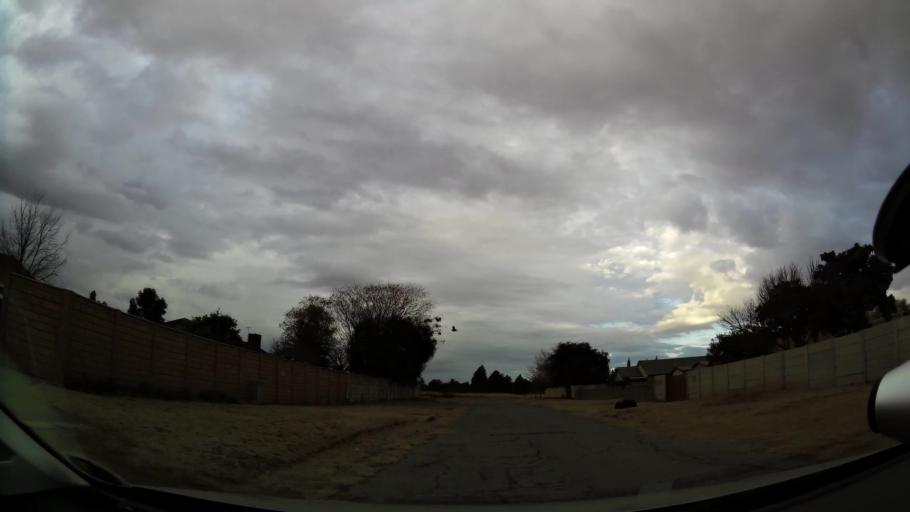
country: ZA
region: Orange Free State
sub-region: Lejweleputswa District Municipality
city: Welkom
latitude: -27.9670
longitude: 26.7211
